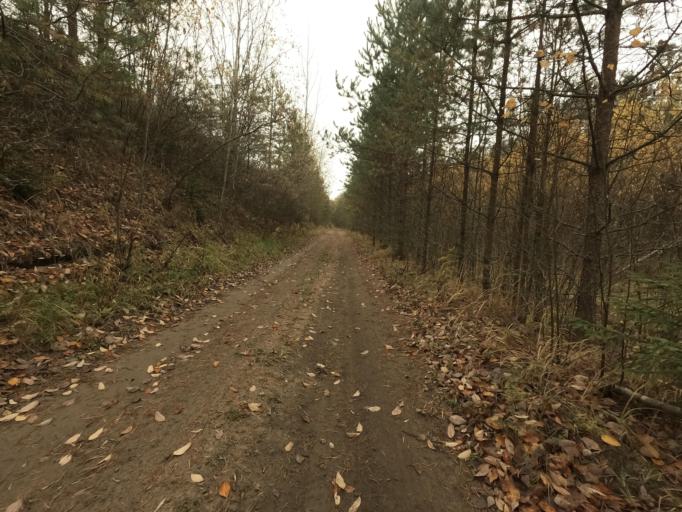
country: RU
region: Leningrad
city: Pavlovo
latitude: 59.7739
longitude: 30.9031
